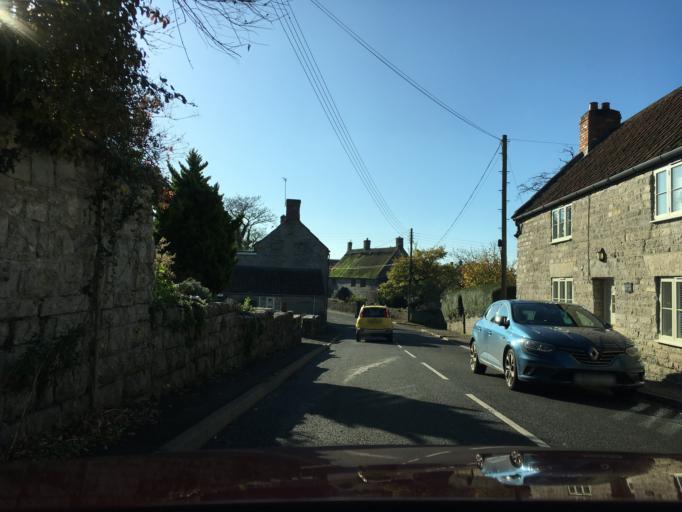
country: GB
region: England
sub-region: Somerset
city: Martock
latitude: 51.0247
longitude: -2.7589
